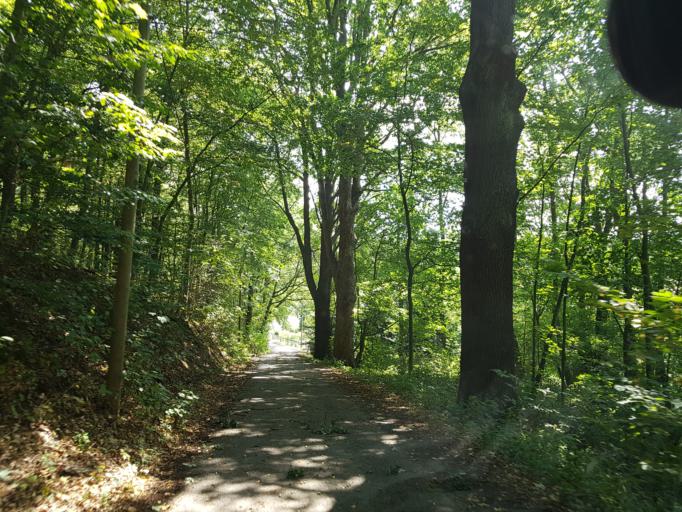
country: DE
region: Saxony
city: Waldheim
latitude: 51.0636
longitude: 13.0075
